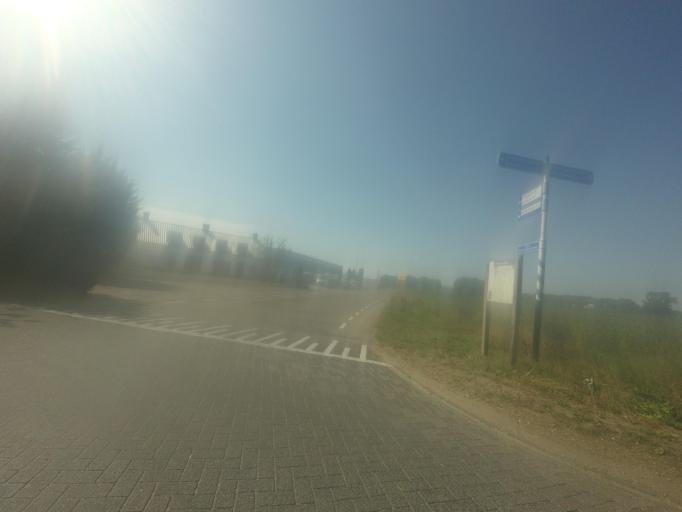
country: NL
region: North Brabant
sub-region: Gemeente Hilvarenbeek
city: Hilvarenbeek
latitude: 51.5129
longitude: 5.1516
